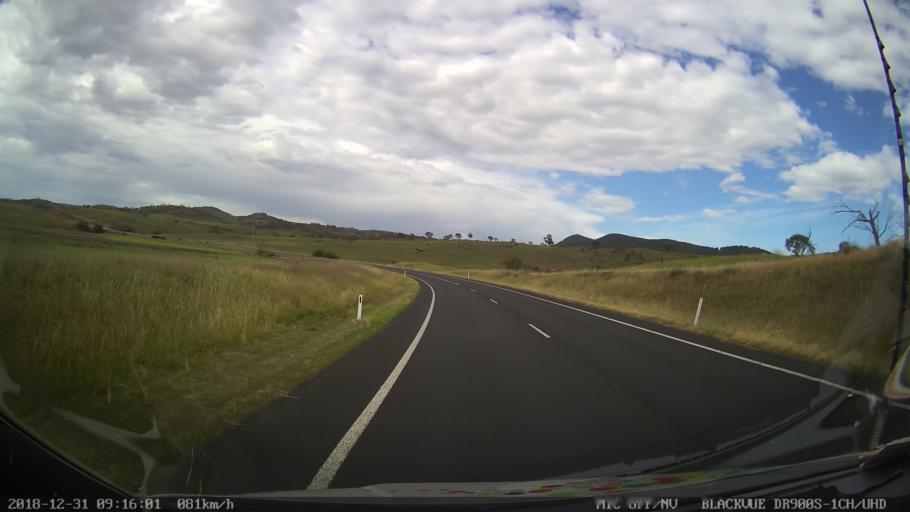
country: AU
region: New South Wales
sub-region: Snowy River
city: Jindabyne
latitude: -36.3914
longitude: 148.5953
